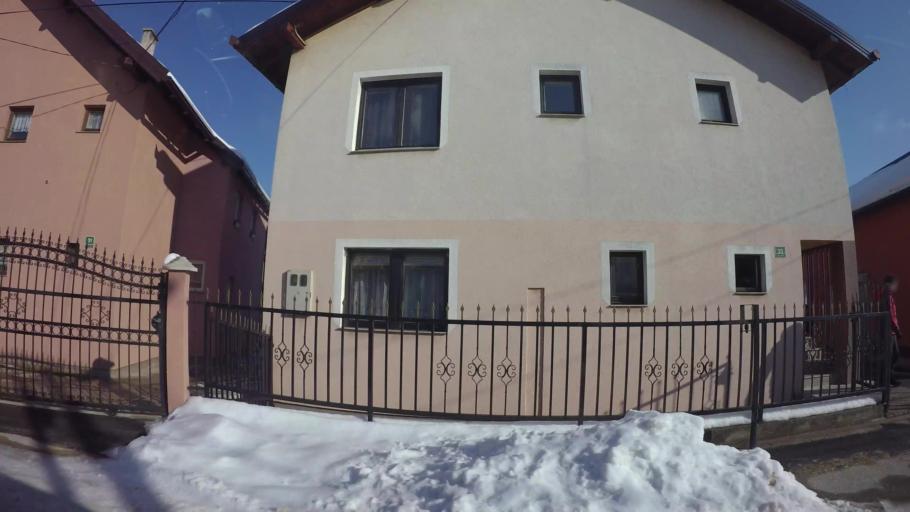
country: BA
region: Federation of Bosnia and Herzegovina
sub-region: Kanton Sarajevo
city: Sarajevo
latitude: 43.8133
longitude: 18.3208
